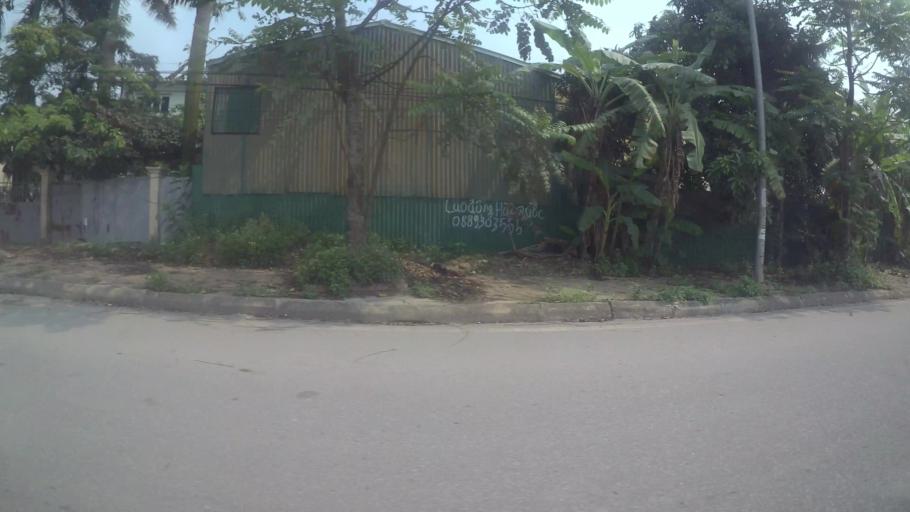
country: VN
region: Ha Noi
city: Quoc Oai
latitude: 21.0015
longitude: 105.6037
